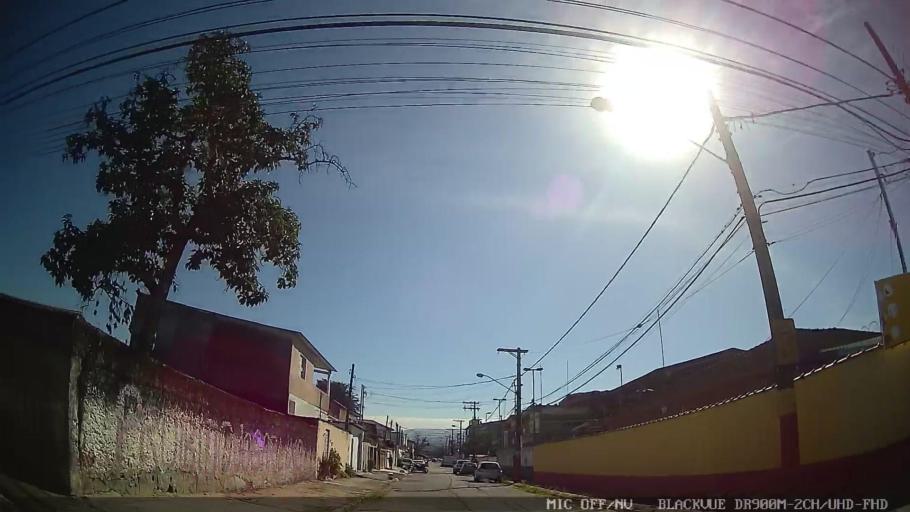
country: BR
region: Sao Paulo
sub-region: Santos
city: Santos
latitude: -23.9428
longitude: -46.2943
